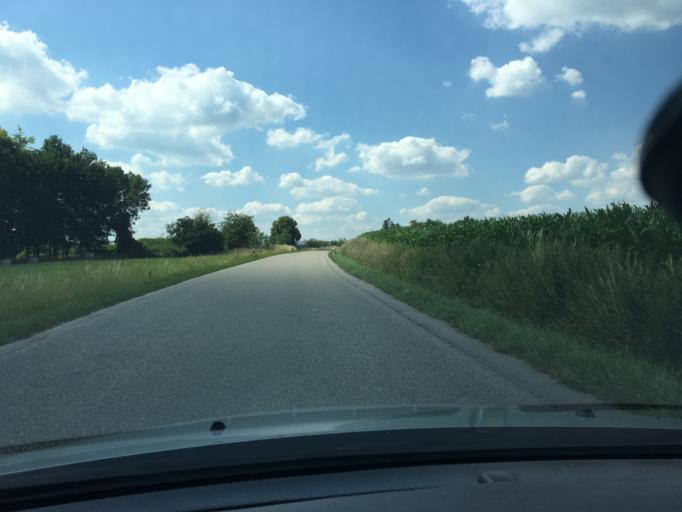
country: DE
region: Bavaria
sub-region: Lower Bavaria
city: Geisenhausen
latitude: 48.4629
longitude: 12.2730
